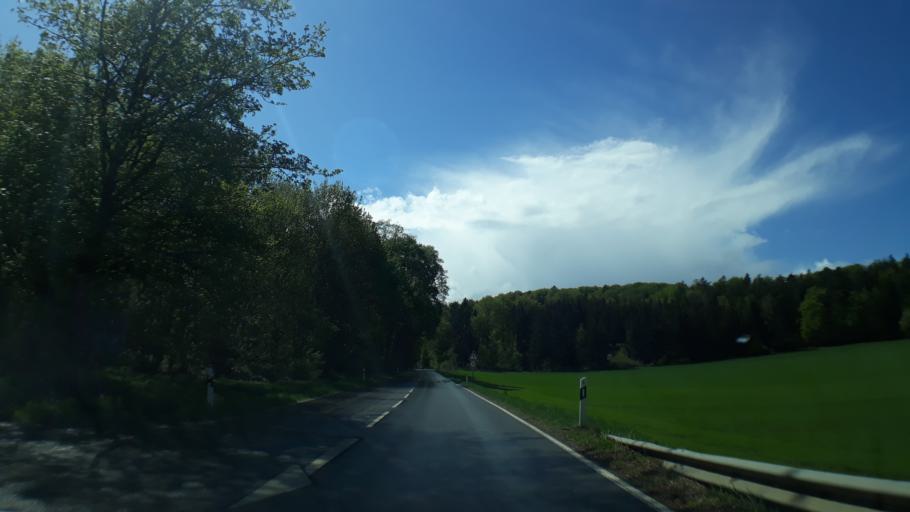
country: DE
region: North Rhine-Westphalia
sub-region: Regierungsbezirk Koln
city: Nettersheim
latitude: 50.5004
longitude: 6.5847
